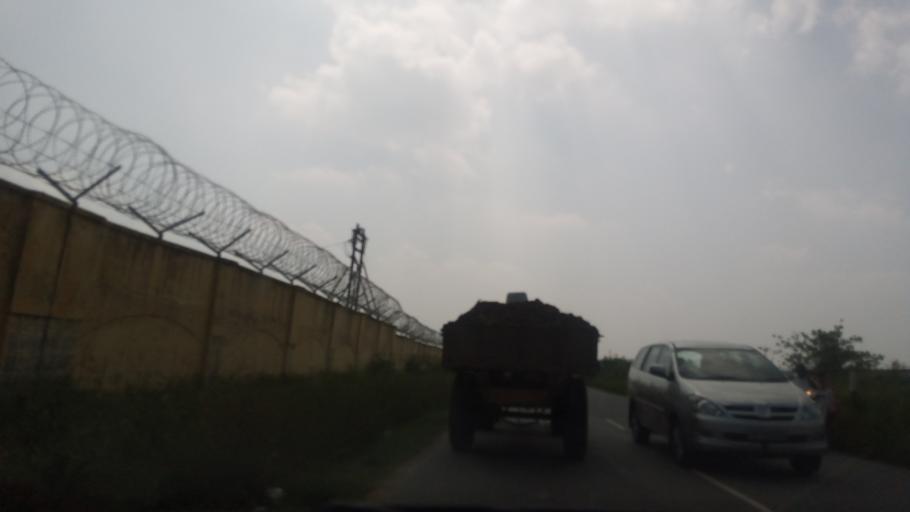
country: IN
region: Tamil Nadu
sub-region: Vellore
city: Arakkonam
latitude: 13.0524
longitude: 79.6742
